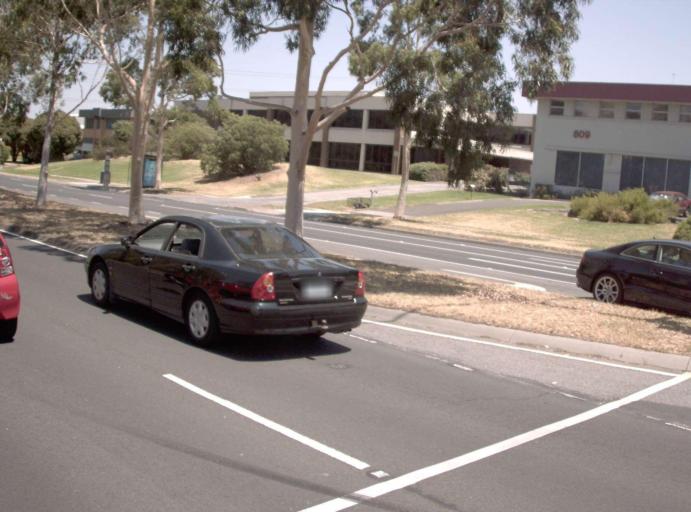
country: AU
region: Victoria
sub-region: Monash
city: Notting Hill
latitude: -37.9241
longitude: 145.1577
